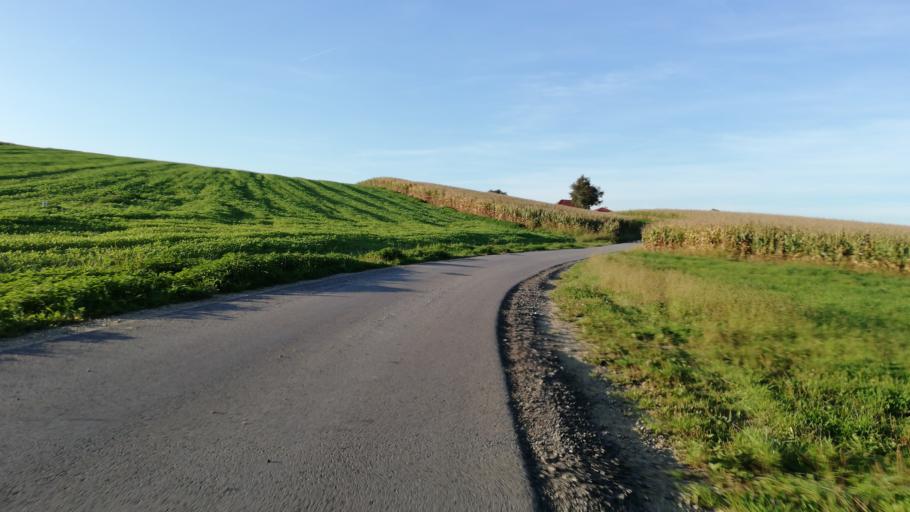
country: AT
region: Upper Austria
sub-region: Wels-Land
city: Edt bei Lambach
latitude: 48.1732
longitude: 13.8931
